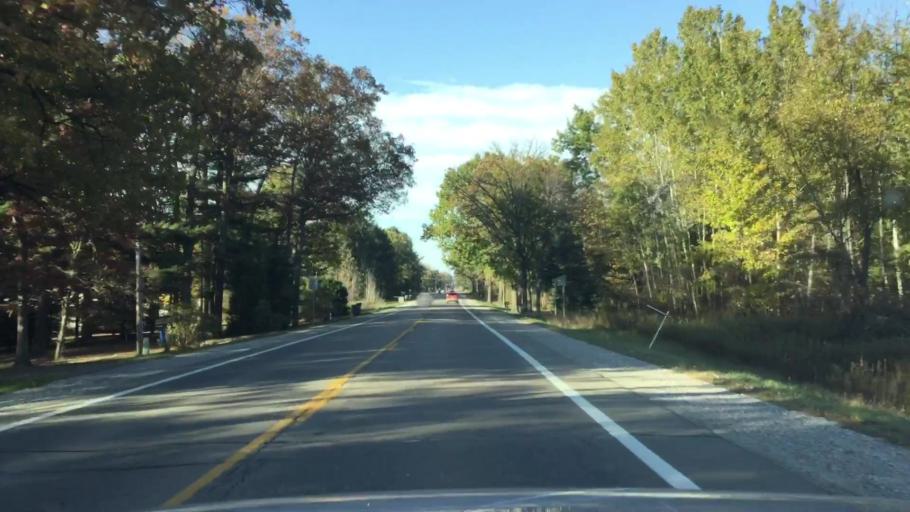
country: US
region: Michigan
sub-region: Lapeer County
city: Barnes Lake-Millers Lake
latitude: 43.1529
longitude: -83.3114
